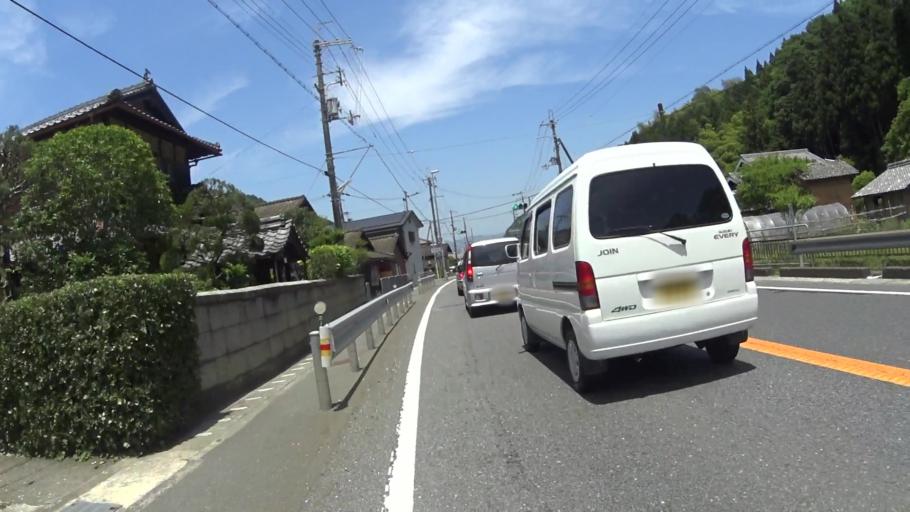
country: JP
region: Kyoto
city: Kameoka
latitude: 35.1389
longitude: 135.4253
